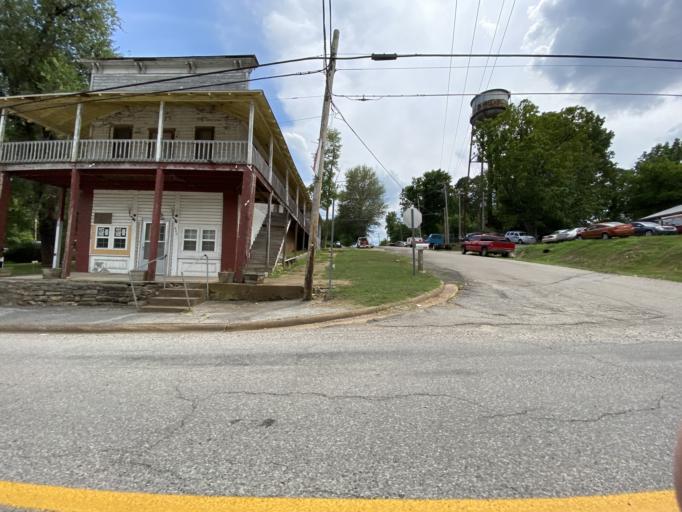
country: US
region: Missouri
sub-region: Oregon County
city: Thayer
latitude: 36.4957
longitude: -91.5428
